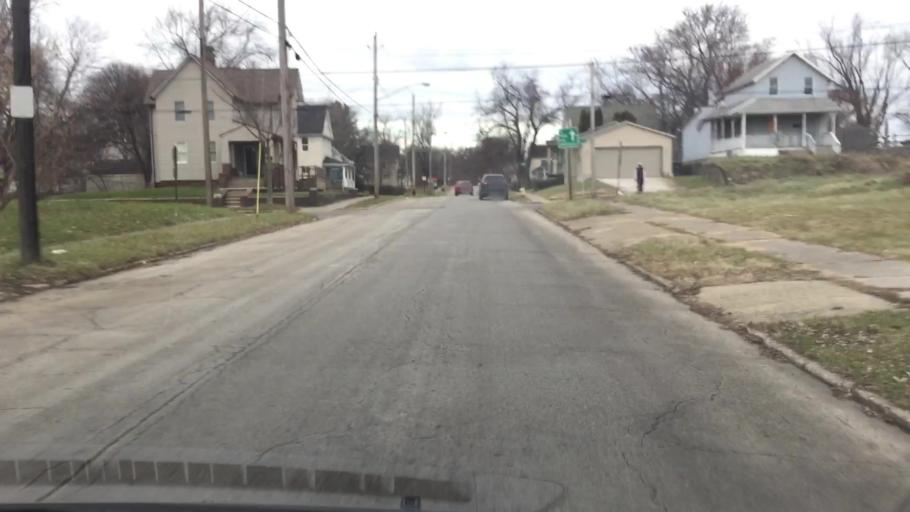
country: US
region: Ohio
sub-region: Summit County
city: Akron
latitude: 41.0550
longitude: -81.5322
